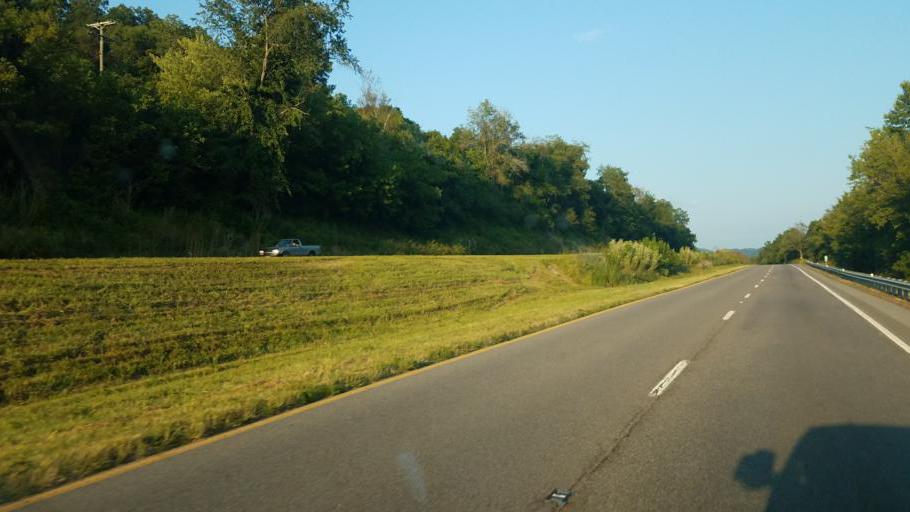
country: US
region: Virginia
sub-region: Scott County
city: Gate City
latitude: 36.6367
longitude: -82.6516
